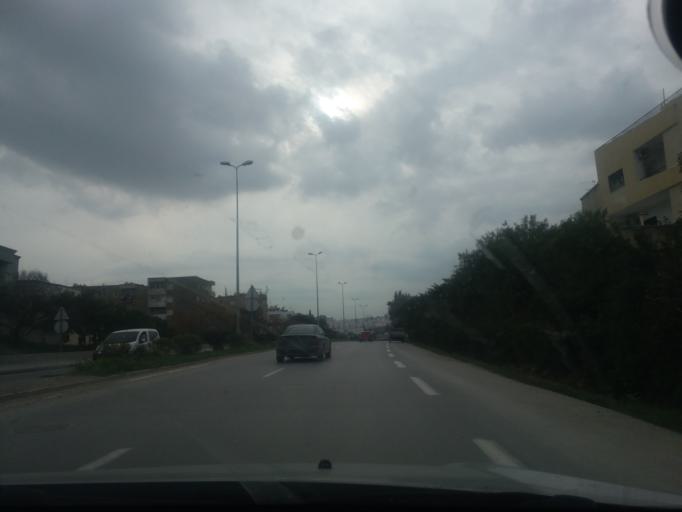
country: TN
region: Ariana
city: Ariana
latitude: 36.8650
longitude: 10.1774
